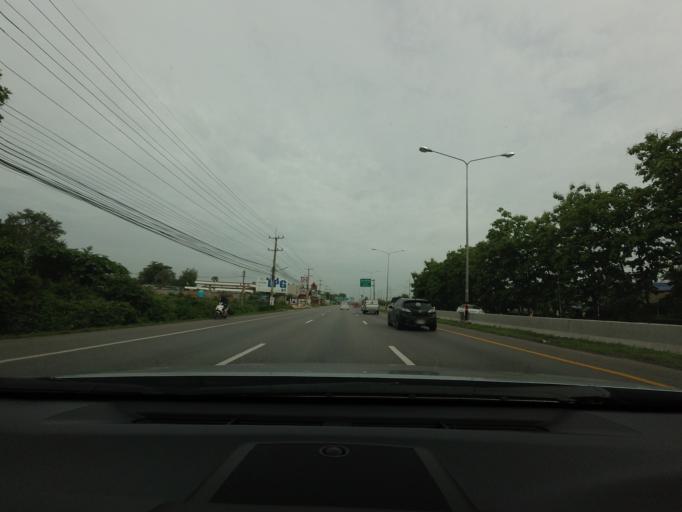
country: TH
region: Phetchaburi
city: Khao Yoi
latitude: 13.1509
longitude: 99.8522
